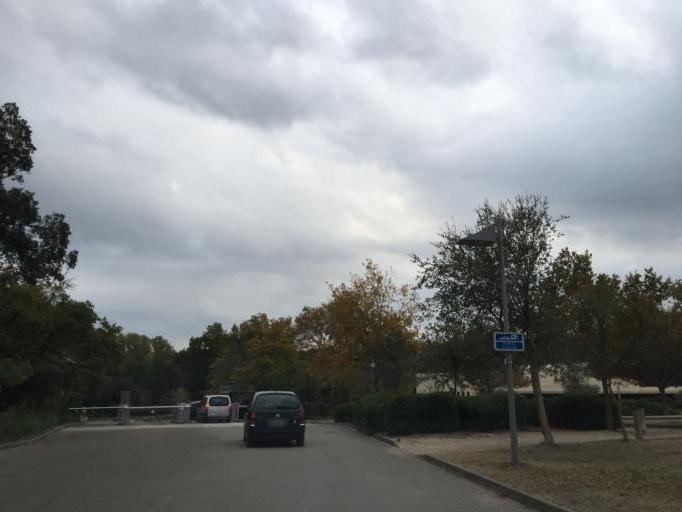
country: FR
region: Languedoc-Roussillon
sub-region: Departement du Gard
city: Castillon-du-Gard
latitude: 43.9531
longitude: 4.5357
